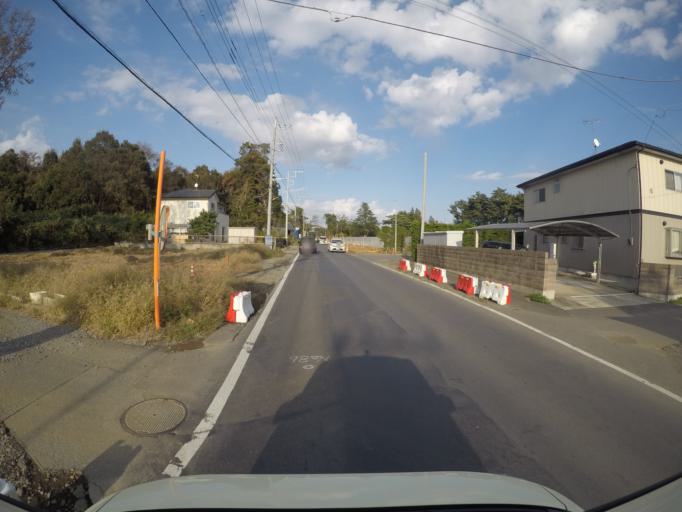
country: JP
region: Ibaraki
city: Mitsukaido
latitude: 36.0020
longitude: 140.0497
